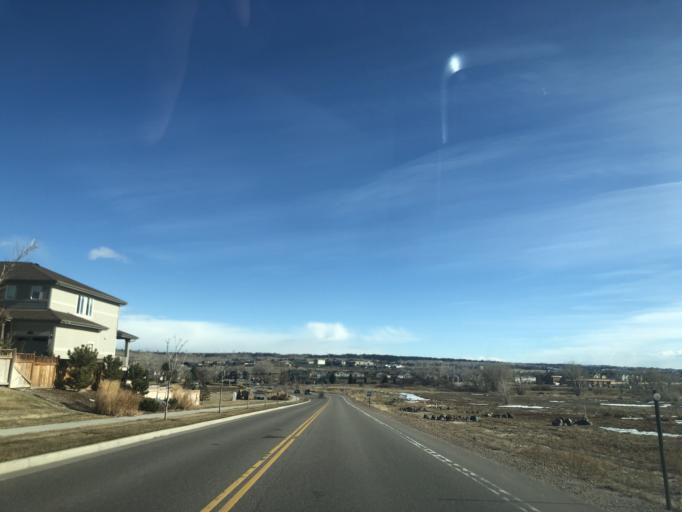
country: US
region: Colorado
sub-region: Douglas County
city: Stonegate
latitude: 39.5540
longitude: -104.7986
